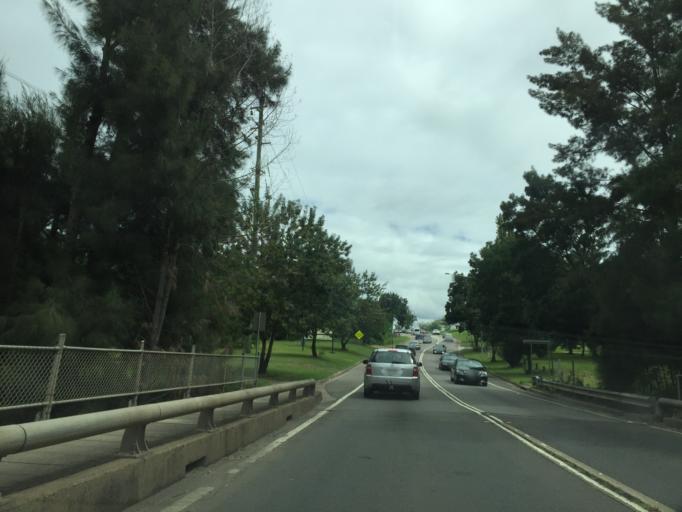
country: AU
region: New South Wales
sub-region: Hawkesbury
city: Richmond
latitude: -33.5844
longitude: 150.7237
